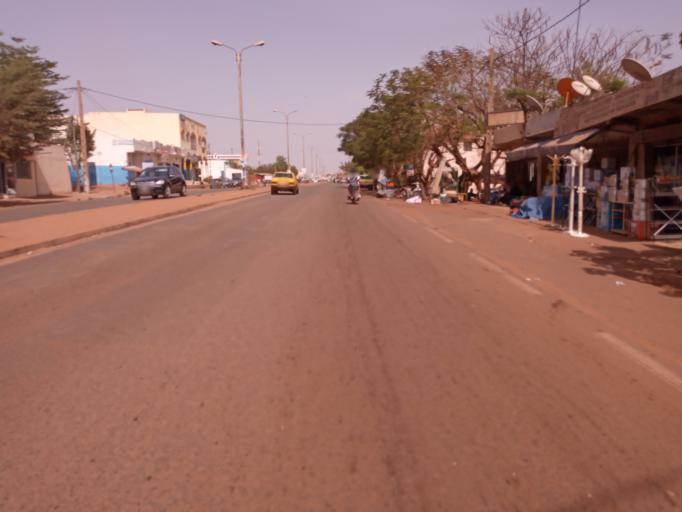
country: ML
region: Bamako
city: Bamako
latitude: 12.5763
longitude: -7.9535
